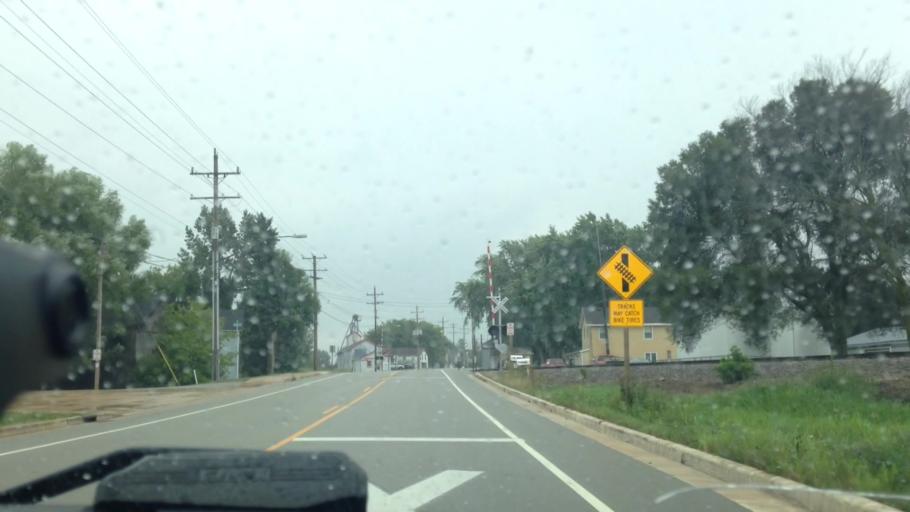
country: US
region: Wisconsin
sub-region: Washington County
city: Richfield
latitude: 43.2602
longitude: -88.1968
